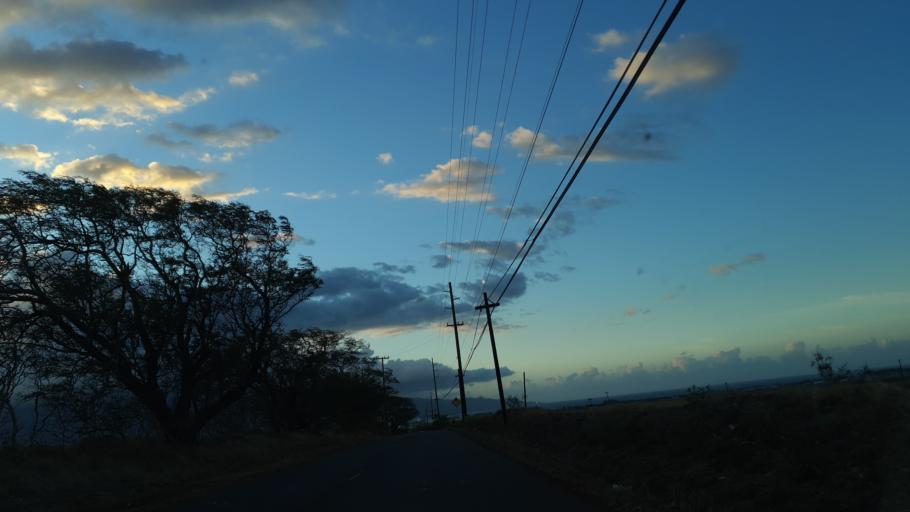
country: US
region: Hawaii
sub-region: Maui County
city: Kahului
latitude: 20.8636
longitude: -156.4298
